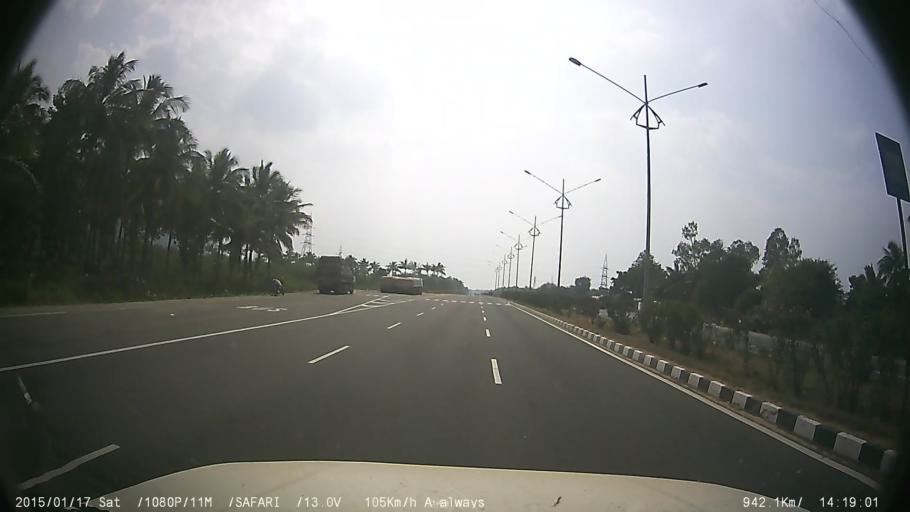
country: IN
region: Tamil Nadu
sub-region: Vellore
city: Vaniyambadi
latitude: 12.7252
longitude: 78.6701
